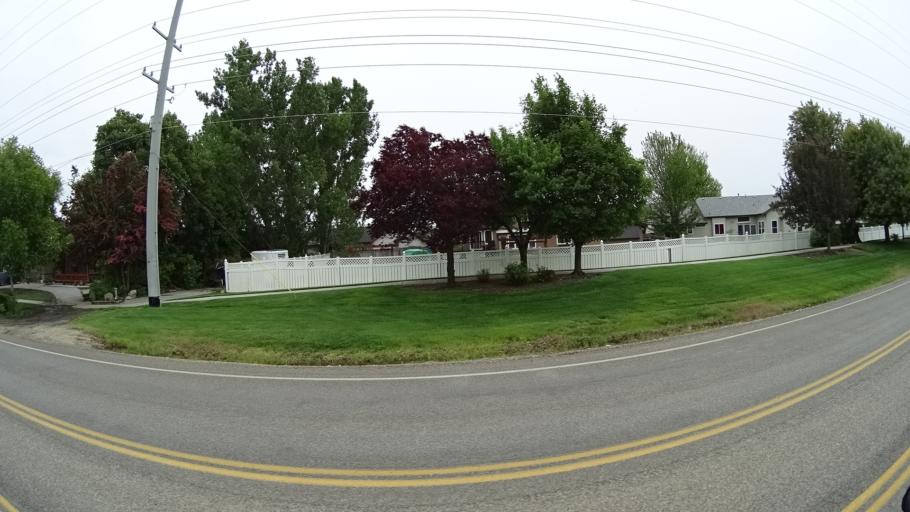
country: US
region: Idaho
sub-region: Ada County
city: Meridian
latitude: 43.6340
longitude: -116.4422
